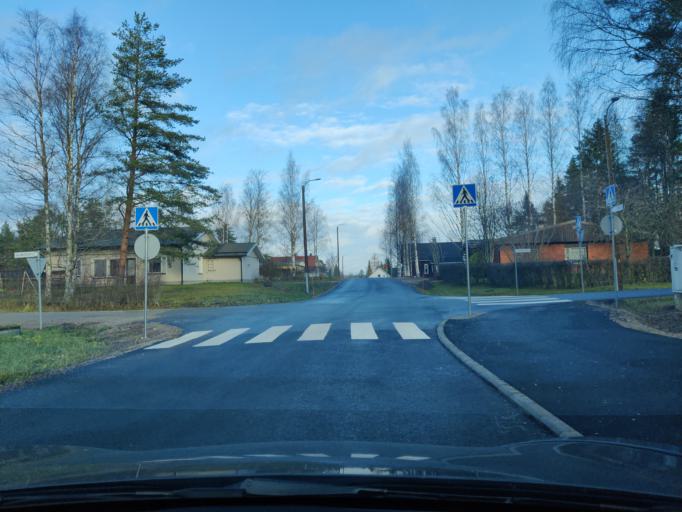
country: FI
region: Northern Savo
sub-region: Ylae-Savo
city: Kiuruvesi
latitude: 63.6476
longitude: 26.6327
